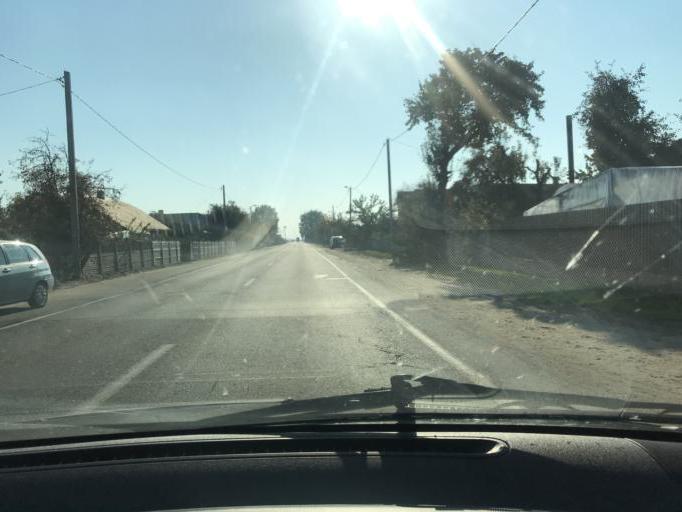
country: BY
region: Brest
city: Davyd-Haradok
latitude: 52.0731
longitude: 27.3392
